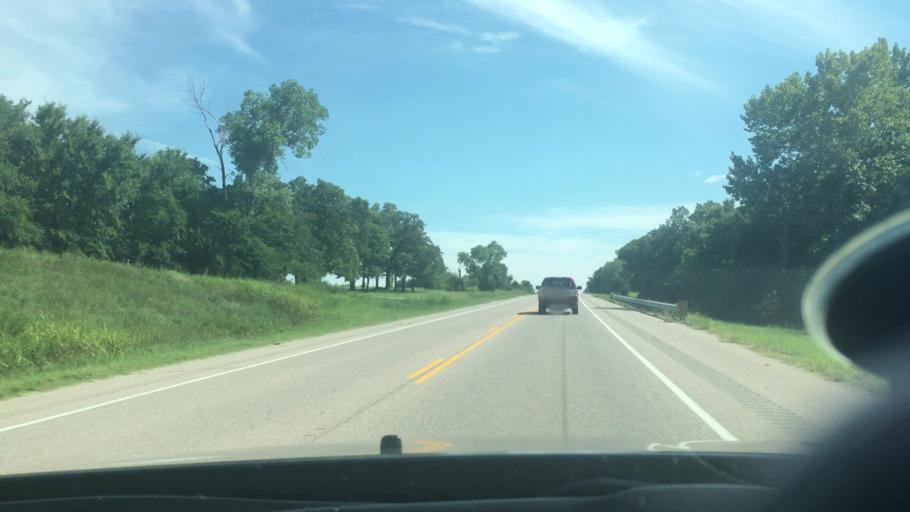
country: US
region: Oklahoma
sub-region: Seminole County
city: Konawa
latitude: 35.0235
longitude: -96.6783
